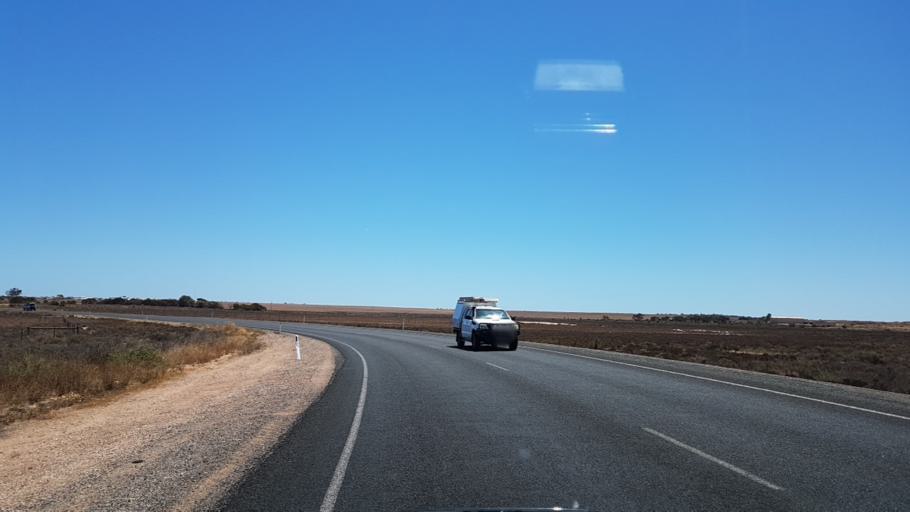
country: AU
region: South Australia
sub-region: Copper Coast
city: Wallaroo
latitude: -33.9155
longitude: 137.6470
